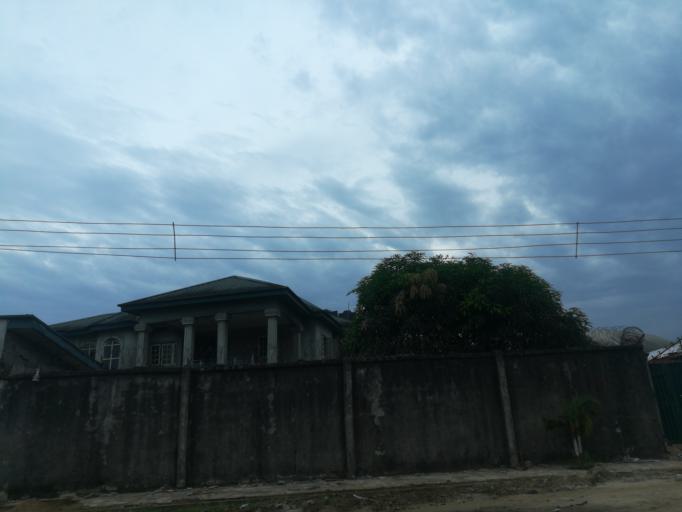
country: NG
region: Rivers
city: Port Harcourt
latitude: 4.7992
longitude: 6.9530
